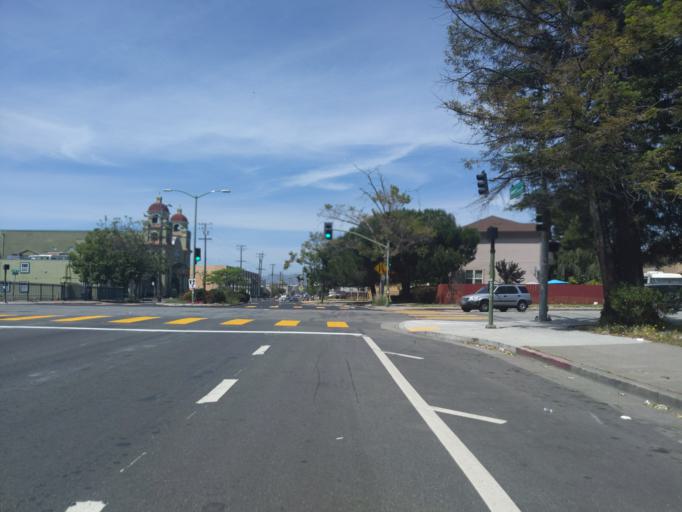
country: US
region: California
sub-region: Alameda County
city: Oakland
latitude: 37.8109
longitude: -122.2798
